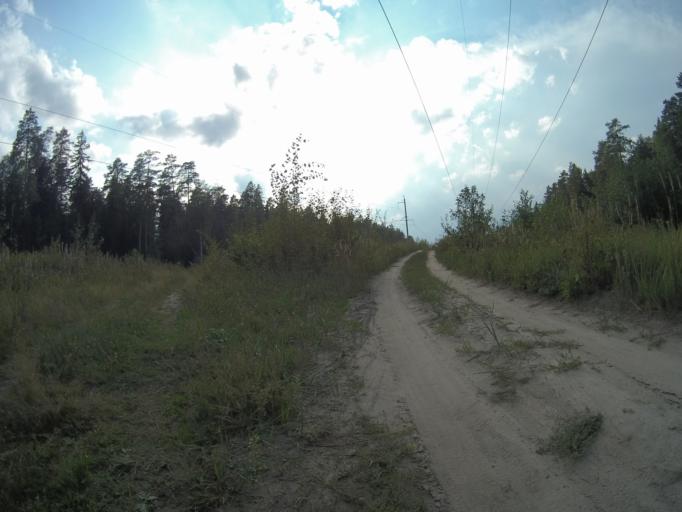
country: RU
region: Vladimir
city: Raduzhnyy
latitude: 56.0140
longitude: 40.2785
